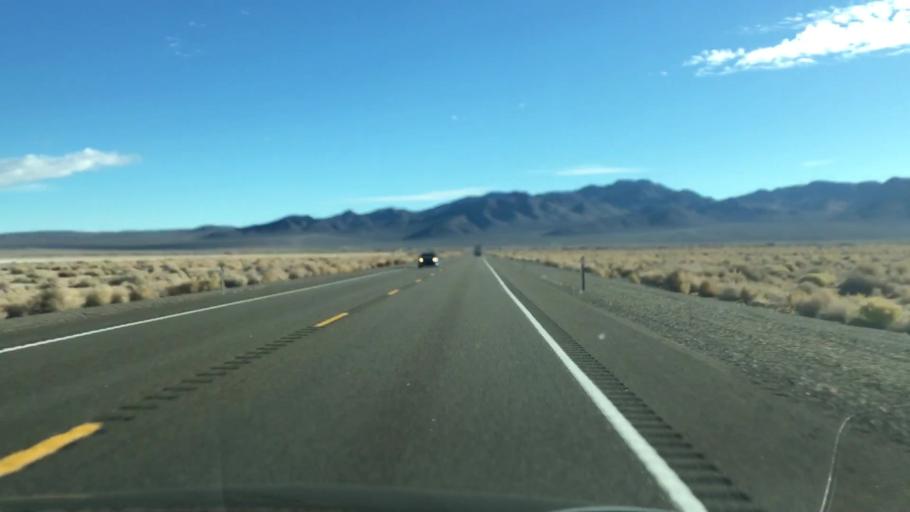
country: US
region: Nevada
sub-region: Mineral County
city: Hawthorne
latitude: 38.2807
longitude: -118.1007
